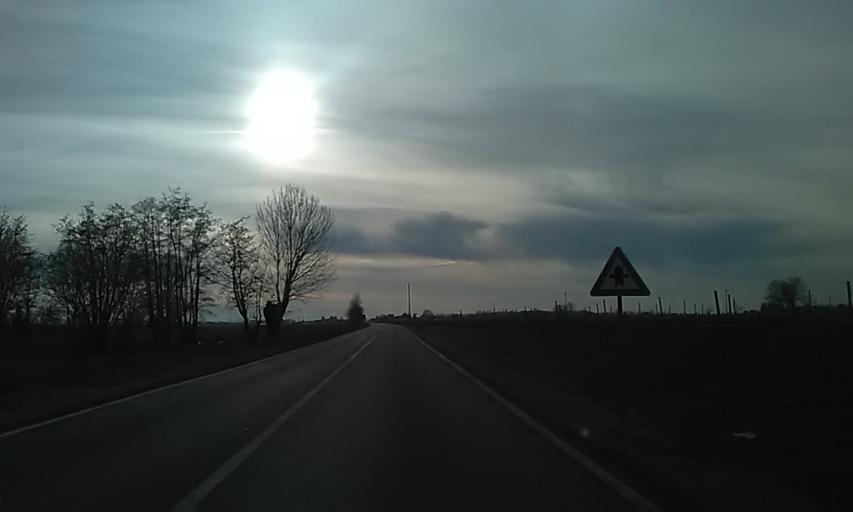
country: IT
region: Piedmont
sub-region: Provincia di Torino
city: Villareggia
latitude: 45.2856
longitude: 7.9926
